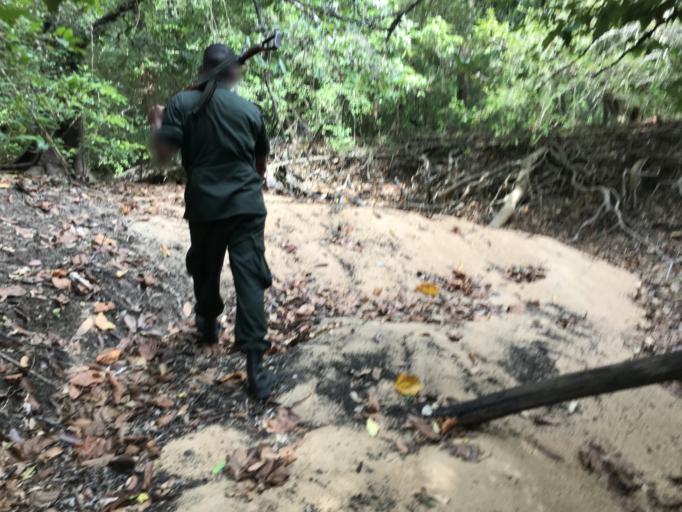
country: LK
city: Padaviya Divisional Secretariat
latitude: 9.0812
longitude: 80.8001
